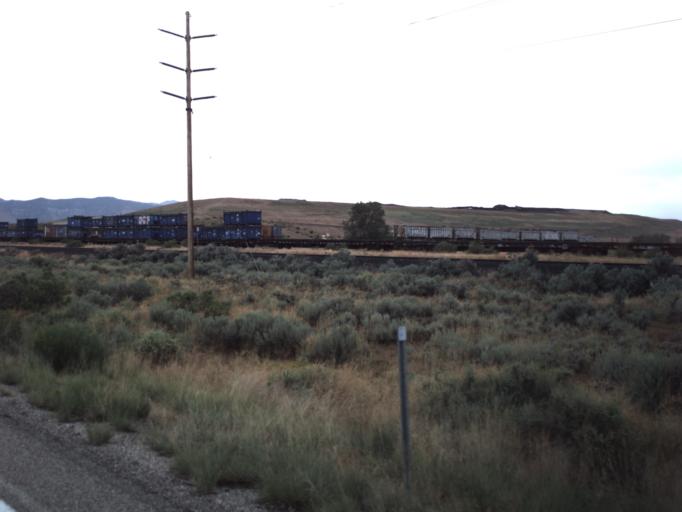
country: US
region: Utah
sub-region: Carbon County
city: East Carbon City
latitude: 39.5356
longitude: -110.4855
